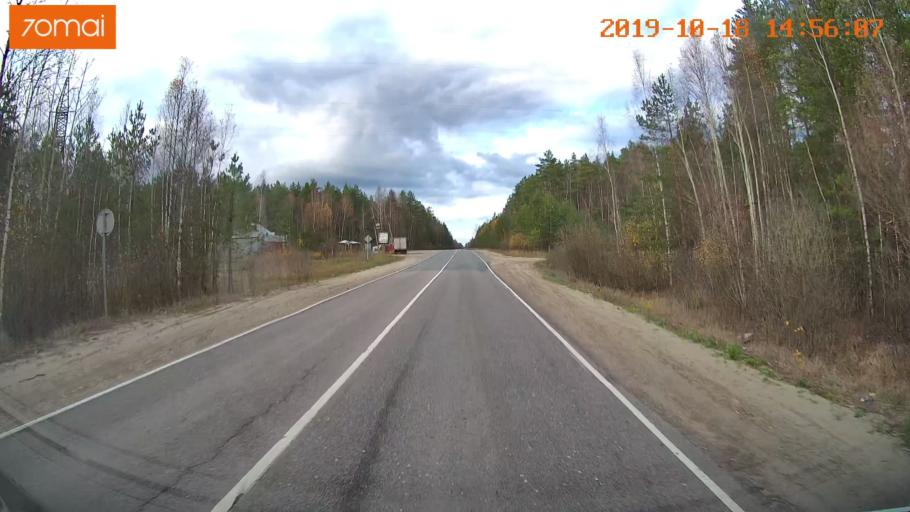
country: RU
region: Vladimir
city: Kurlovo
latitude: 55.4606
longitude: 40.5890
